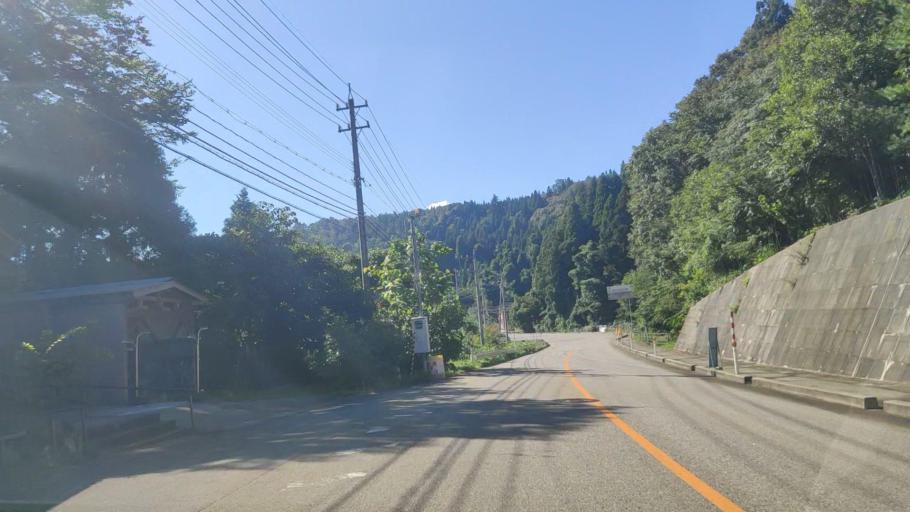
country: JP
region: Ishikawa
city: Nanao
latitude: 37.3403
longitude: 137.2227
